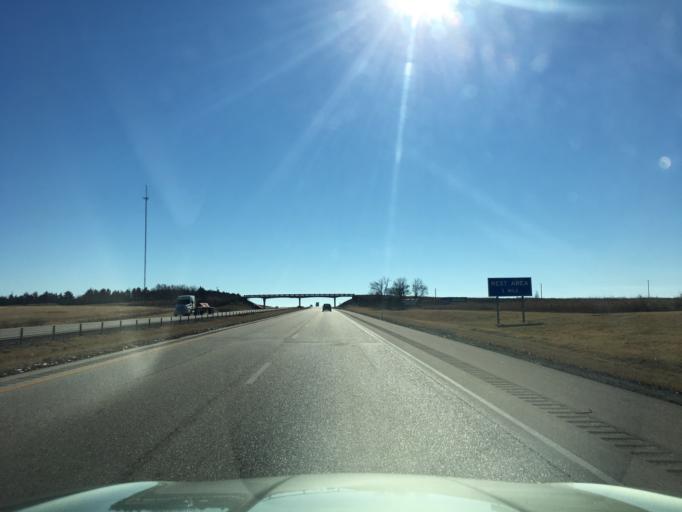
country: US
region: Oklahoma
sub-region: Kay County
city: Blackwell
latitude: 36.8721
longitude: -97.3494
